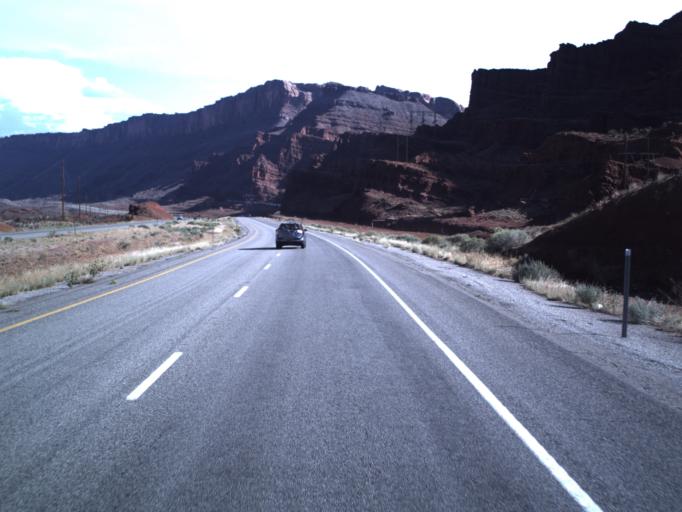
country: US
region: Utah
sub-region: Grand County
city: Moab
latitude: 38.6423
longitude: -109.6685
